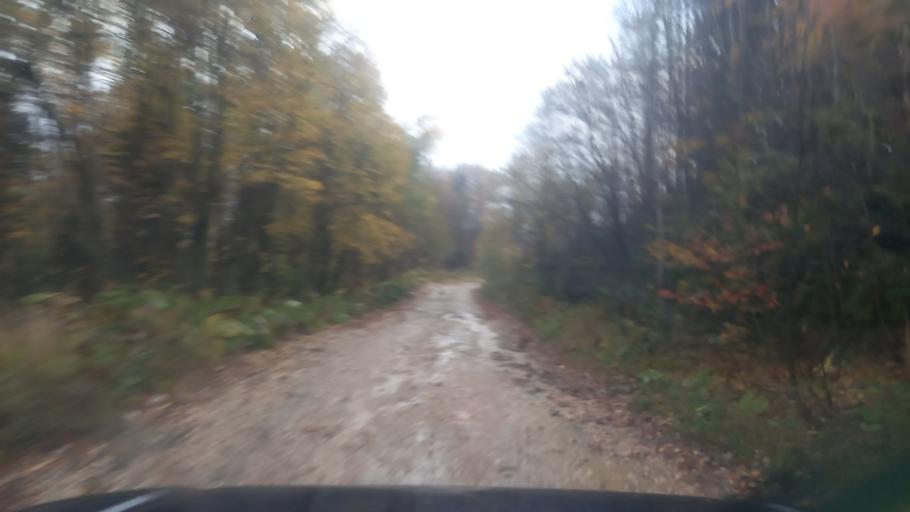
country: RU
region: Krasnodarskiy
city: Neftegorsk
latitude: 44.0156
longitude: 39.8437
